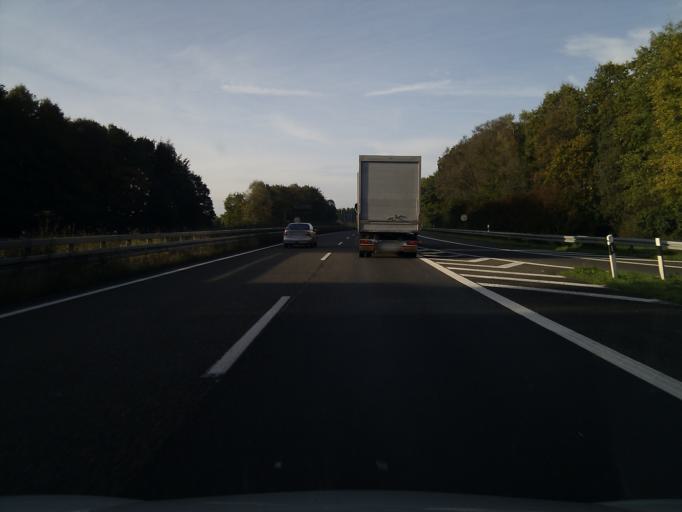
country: BE
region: Wallonia
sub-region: Province de Liege
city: Raeren
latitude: 50.7223
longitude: 6.1278
